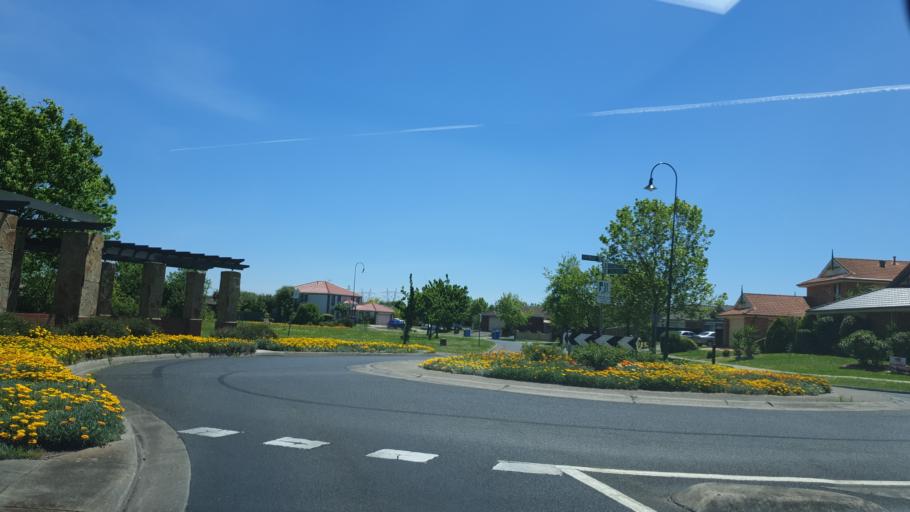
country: AU
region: Victoria
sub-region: Casey
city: Narre Warren South
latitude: -38.0611
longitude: 145.2858
